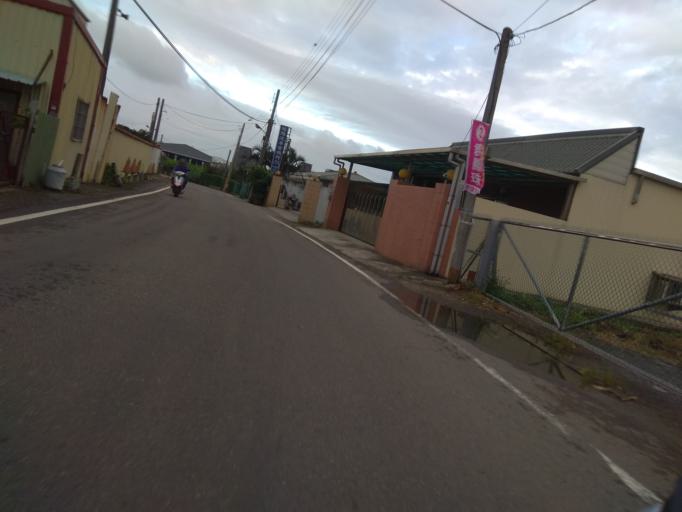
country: TW
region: Taiwan
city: Daxi
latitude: 24.9386
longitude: 121.1946
